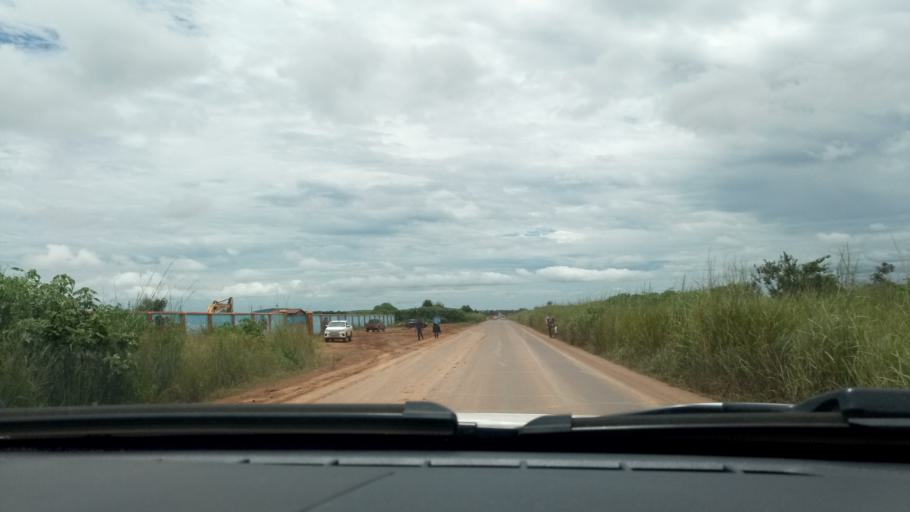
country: CD
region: Katanga
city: Lubumbashi
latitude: -11.5730
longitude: 27.5408
